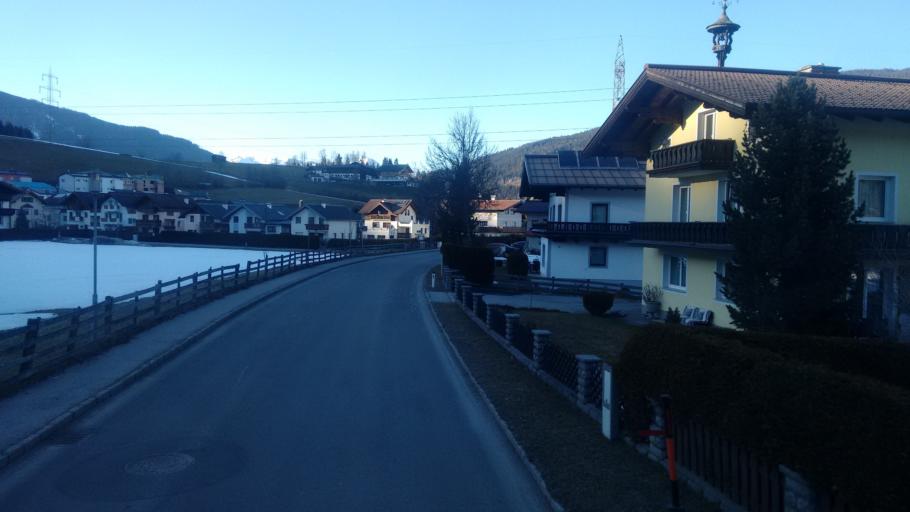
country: AT
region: Salzburg
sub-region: Politischer Bezirk Sankt Johann im Pongau
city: Altenmarkt im Pongau
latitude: 47.3708
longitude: 13.4211
